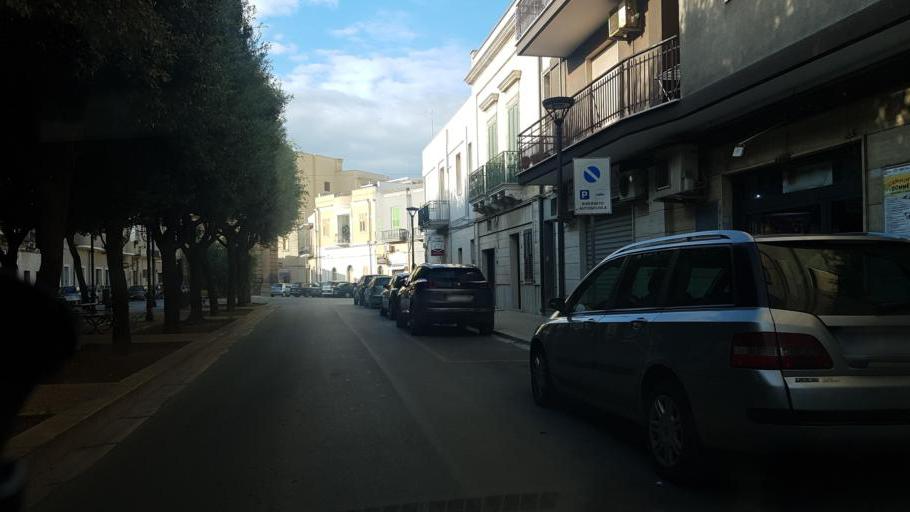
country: IT
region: Apulia
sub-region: Provincia di Brindisi
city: Francavilla Fontana
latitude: 40.5282
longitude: 17.5871
